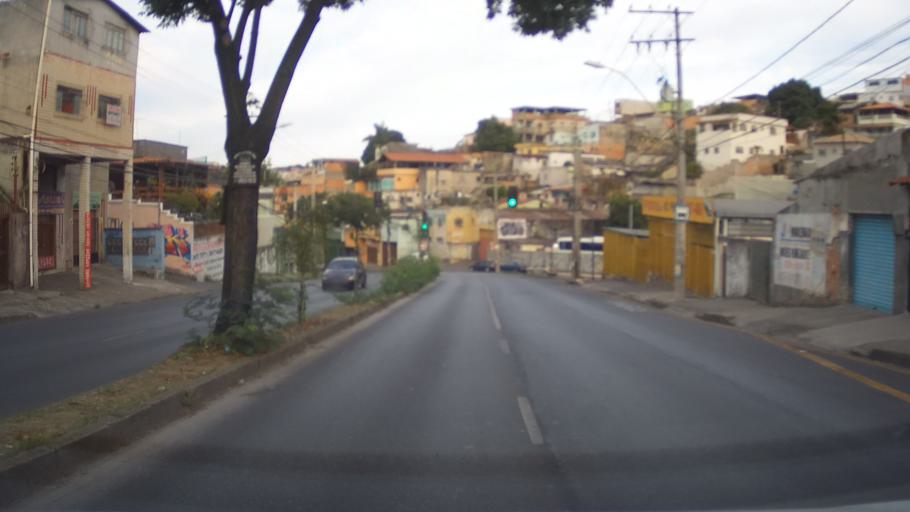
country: BR
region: Minas Gerais
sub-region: Belo Horizonte
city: Belo Horizonte
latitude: -19.9140
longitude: -43.9966
